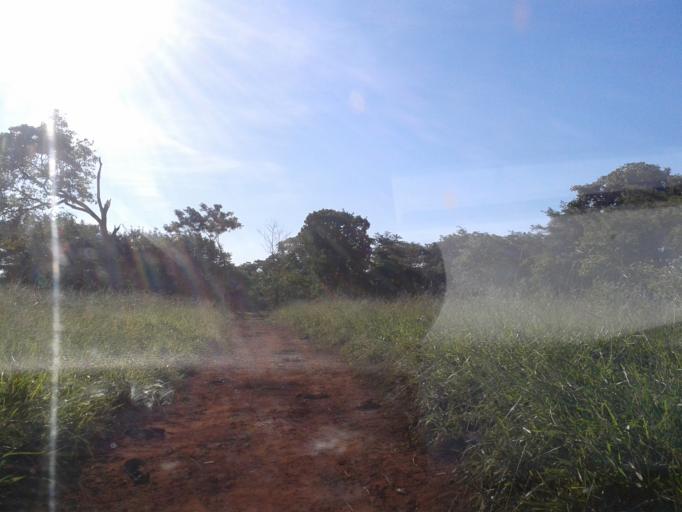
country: BR
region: Minas Gerais
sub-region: Santa Vitoria
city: Santa Vitoria
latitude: -18.9907
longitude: -50.3510
